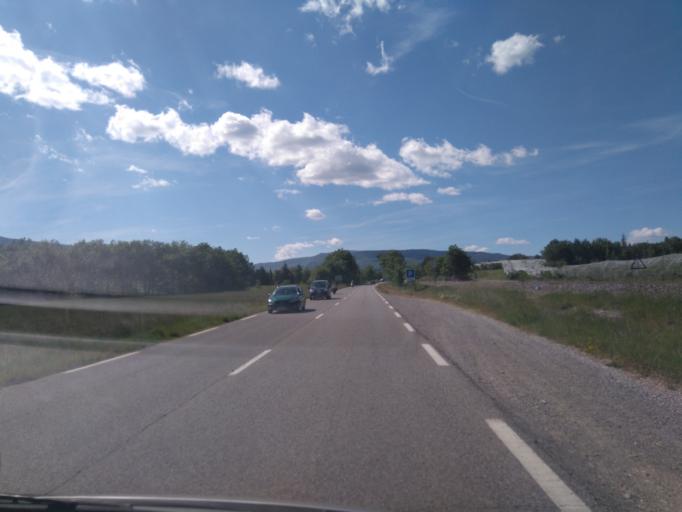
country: FR
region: Provence-Alpes-Cote d'Azur
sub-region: Departement des Hautes-Alpes
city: Laragne-Monteglin
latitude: 44.2537
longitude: 5.8756
